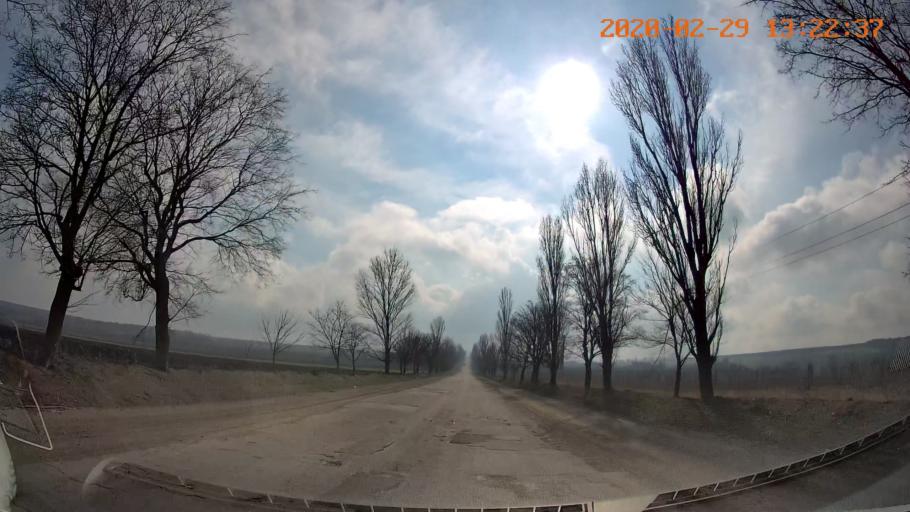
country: MD
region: Telenesti
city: Camenca
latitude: 47.9584
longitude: 28.6275
